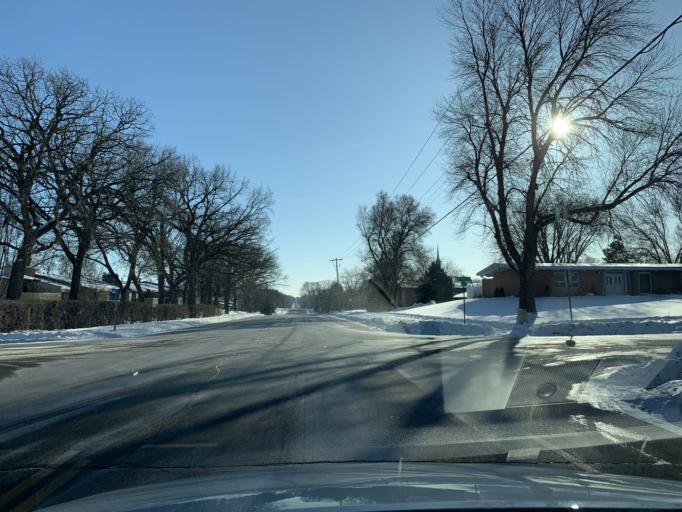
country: US
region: Minnesota
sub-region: Scott County
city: Savage
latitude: 44.8298
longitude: -93.3585
